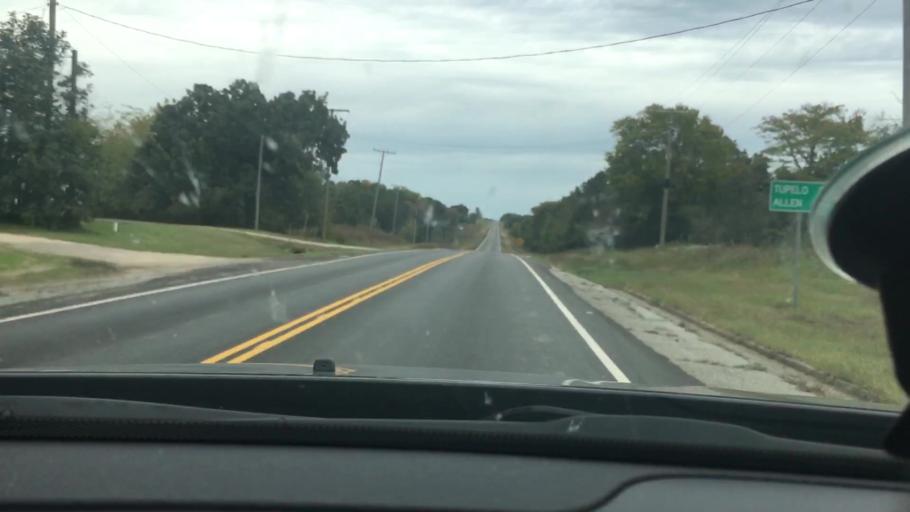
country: US
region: Oklahoma
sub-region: Coal County
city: Coalgate
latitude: 34.3783
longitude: -96.4245
